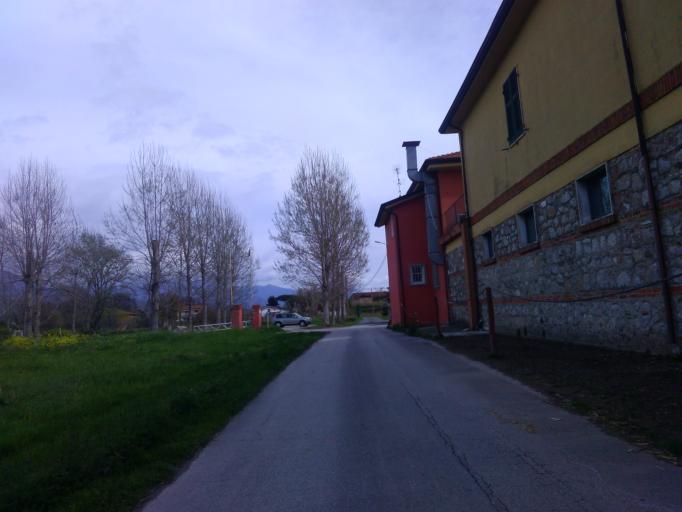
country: IT
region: Liguria
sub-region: Provincia di La Spezia
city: Casano-Dogana-Isola
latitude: 44.0560
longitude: 10.0285
